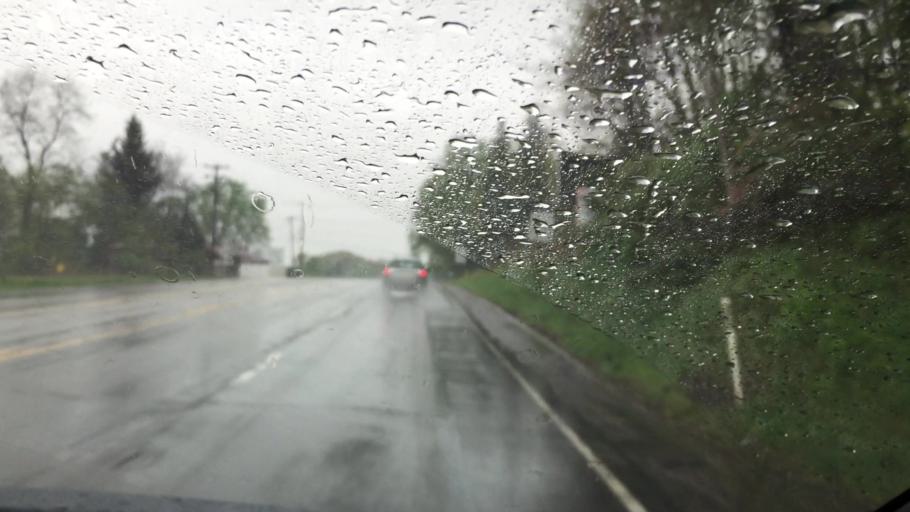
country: US
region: Pennsylvania
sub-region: Butler County
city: Nixon
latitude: 40.7492
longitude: -79.9250
